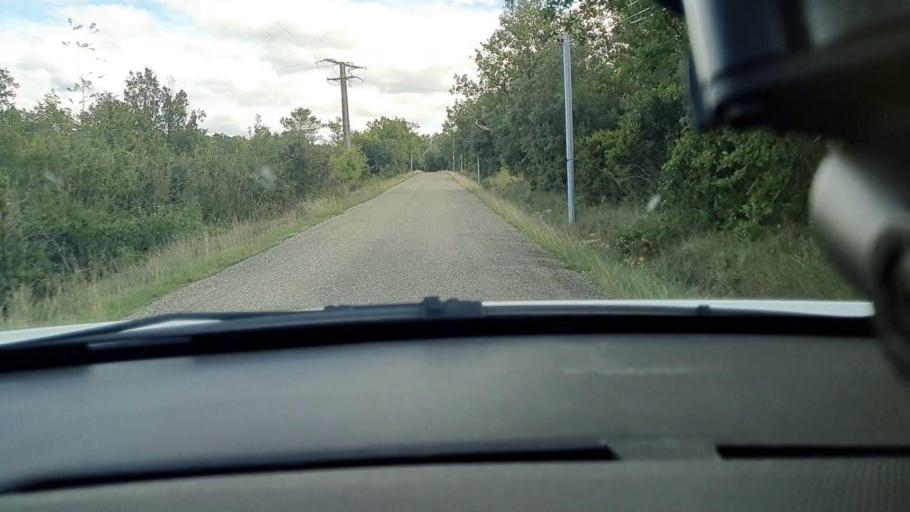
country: FR
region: Languedoc-Roussillon
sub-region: Departement du Gard
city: Mons
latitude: 44.1660
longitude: 4.3031
